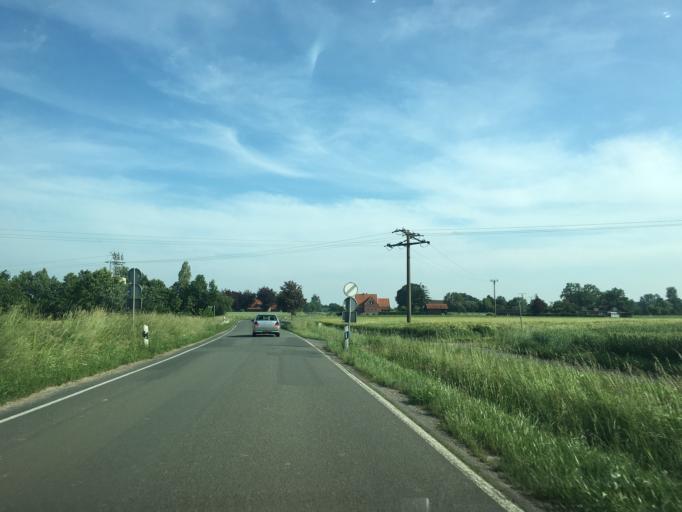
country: DE
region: North Rhine-Westphalia
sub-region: Regierungsbezirk Munster
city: Nordwalde
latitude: 52.1139
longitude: 7.4577
